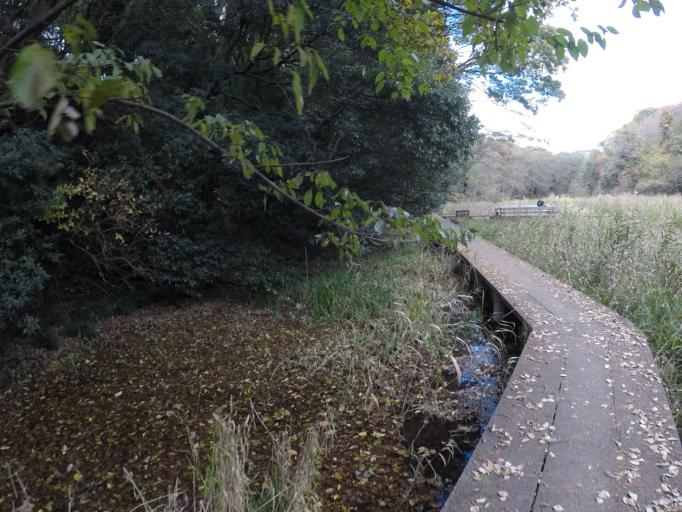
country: JP
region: Chiba
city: Matsudo
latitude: 35.7707
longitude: 139.9700
